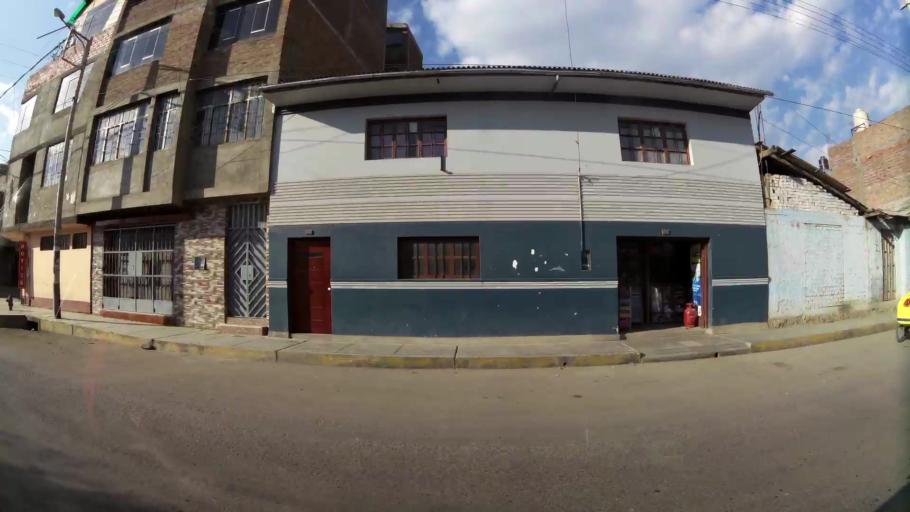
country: PE
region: Junin
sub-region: Provincia de Huancayo
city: El Tambo
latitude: -12.0445
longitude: -75.2186
